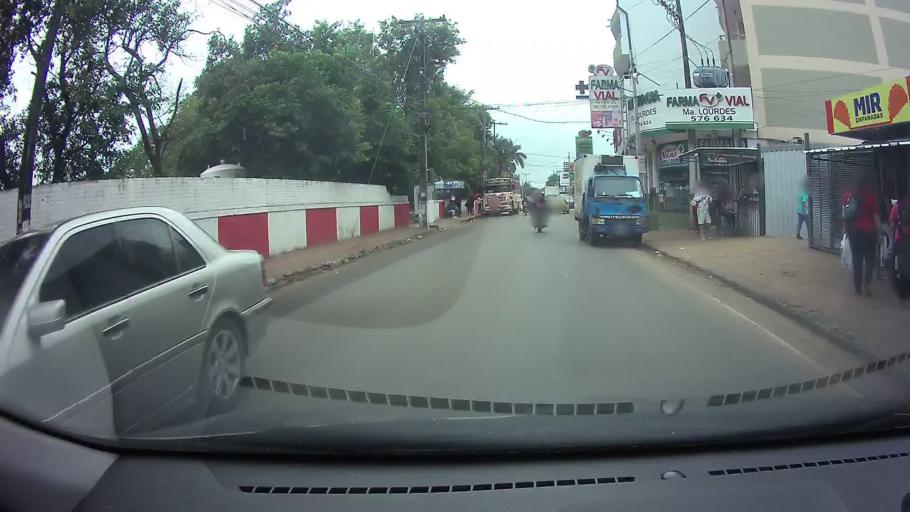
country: PY
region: Central
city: San Lorenzo
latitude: -25.3358
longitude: -57.5086
